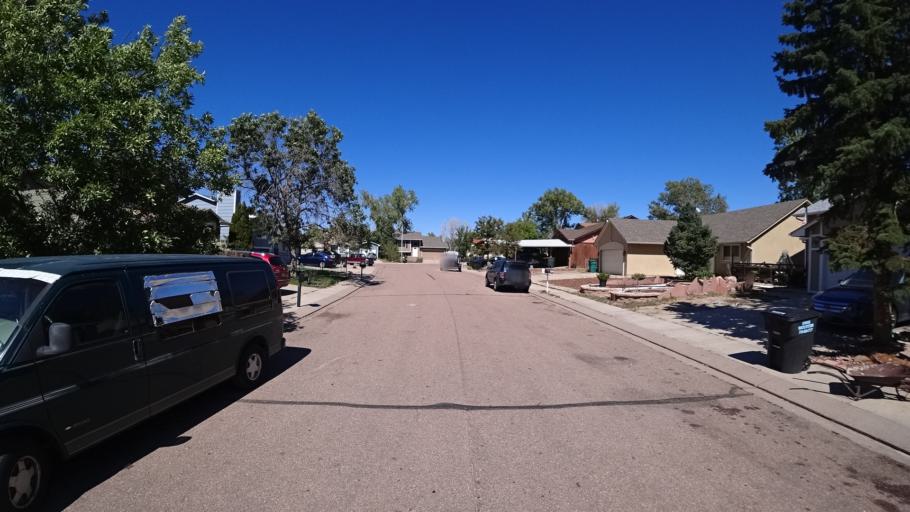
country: US
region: Colorado
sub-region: El Paso County
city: Stratmoor
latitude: 38.7879
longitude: -104.7445
